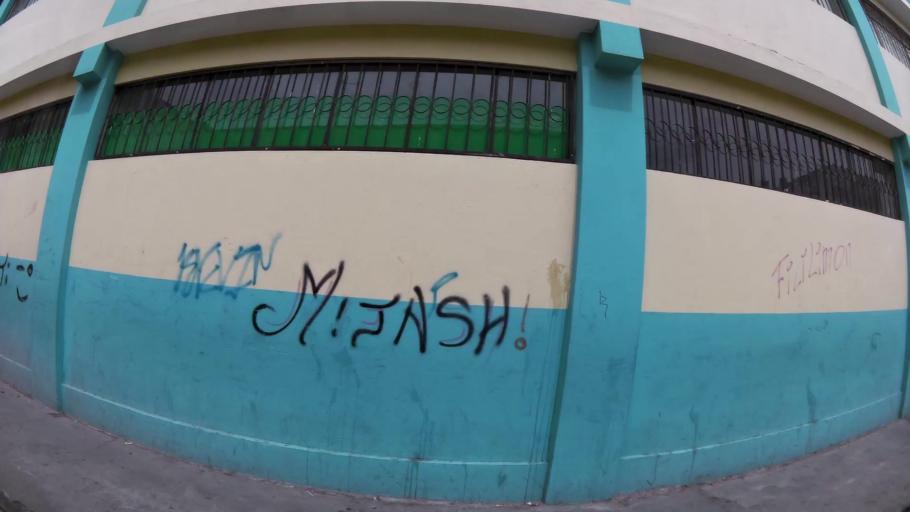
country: EC
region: Cotopaxi
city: Latacunga
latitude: -0.9295
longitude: -78.6166
